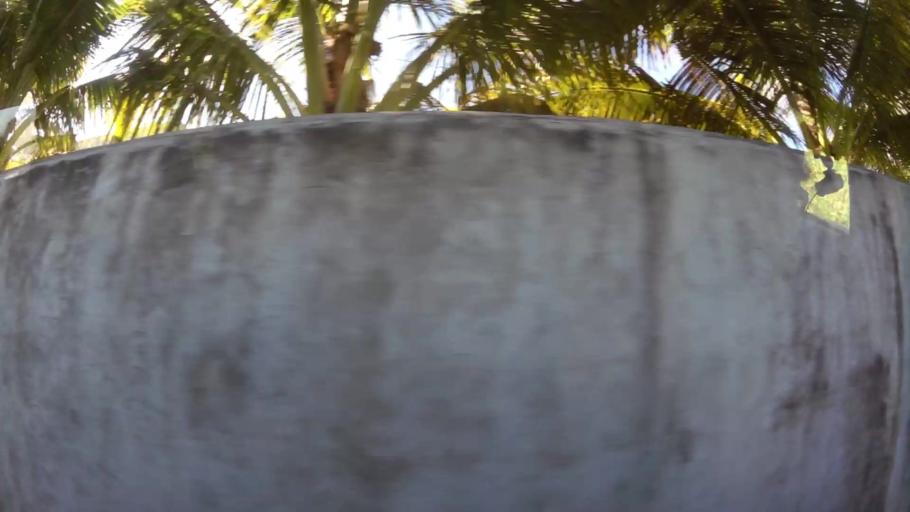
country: GT
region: Santa Rosa
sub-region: Municipio de Taxisco
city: Taxisco
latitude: 13.8684
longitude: -90.4173
